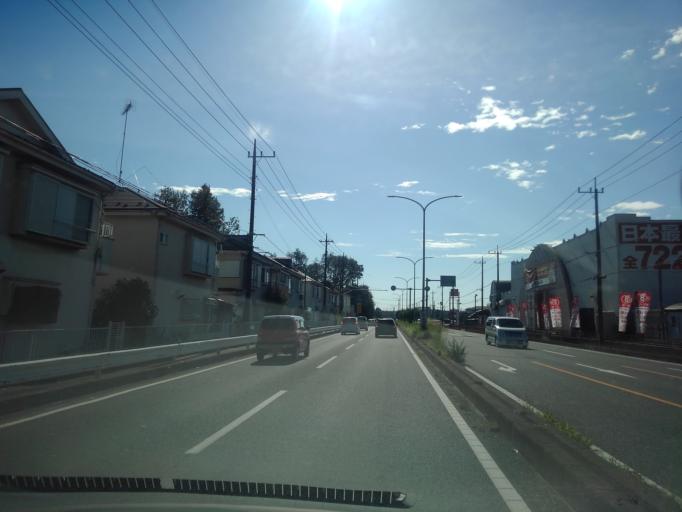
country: JP
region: Saitama
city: Sayama
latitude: 35.8193
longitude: 139.3886
